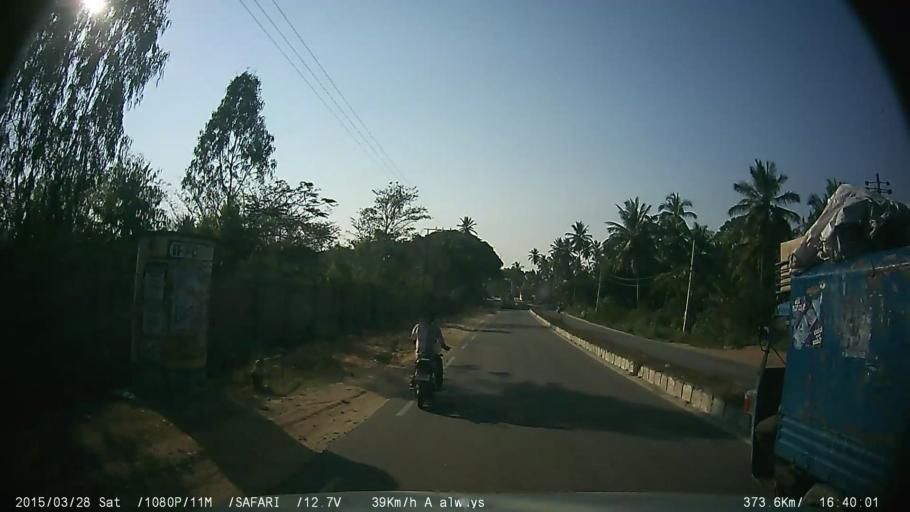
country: IN
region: Karnataka
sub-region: Mandya
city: Shrirangapattana
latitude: 12.3916
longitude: 76.5882
